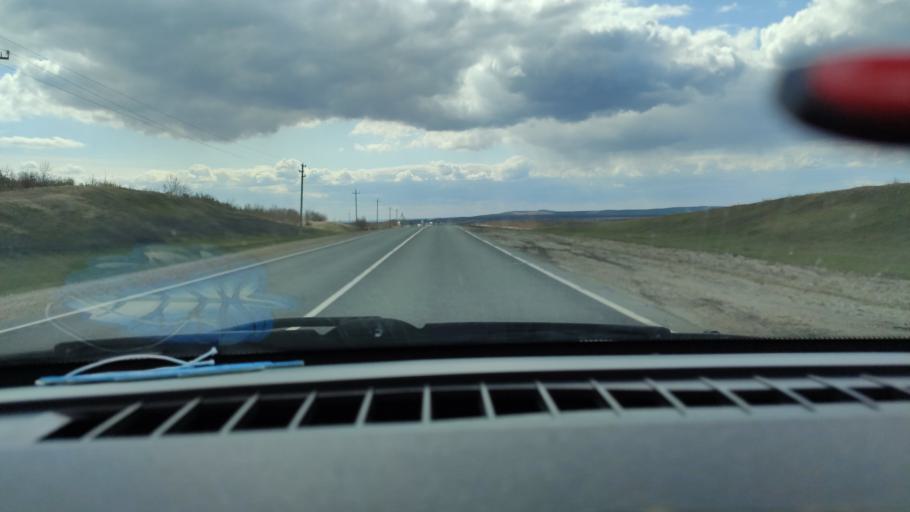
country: RU
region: Saratov
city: Alekseyevka
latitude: 52.2963
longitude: 47.9283
